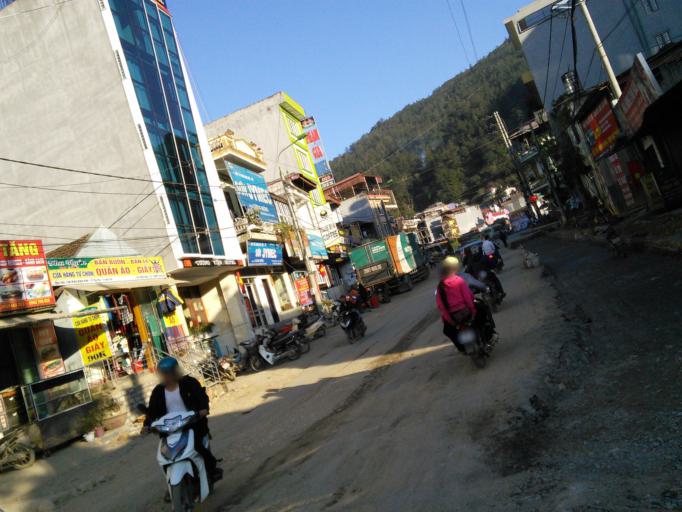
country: VN
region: Lao Cai
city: Sa Pa
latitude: 22.3391
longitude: 103.8503
